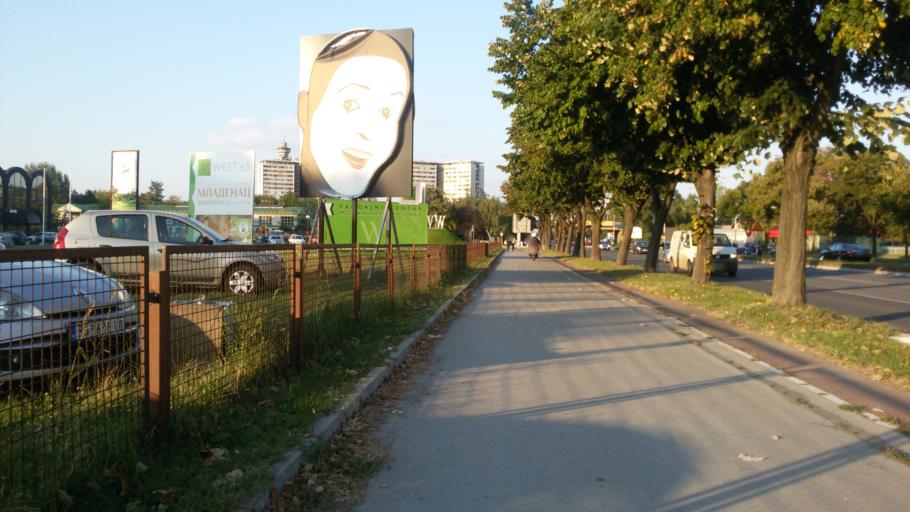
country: RS
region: Central Serbia
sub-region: Belgrade
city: Novi Beograd
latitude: 44.8118
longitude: 20.4017
